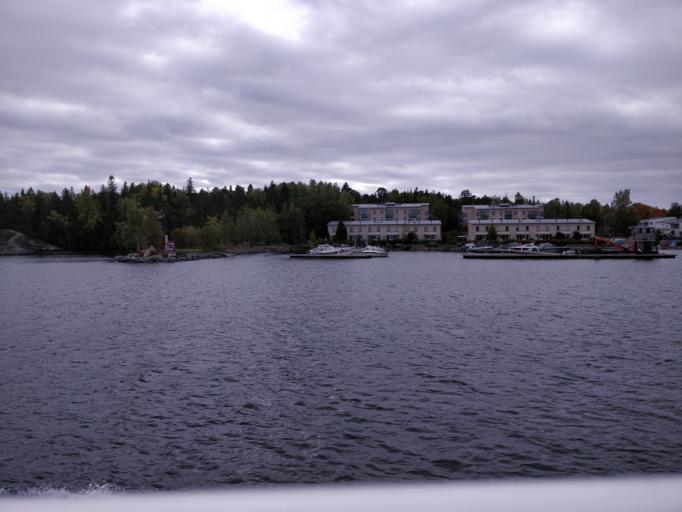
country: FI
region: Uusimaa
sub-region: Helsinki
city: Vantaa
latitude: 60.1736
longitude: 25.0856
